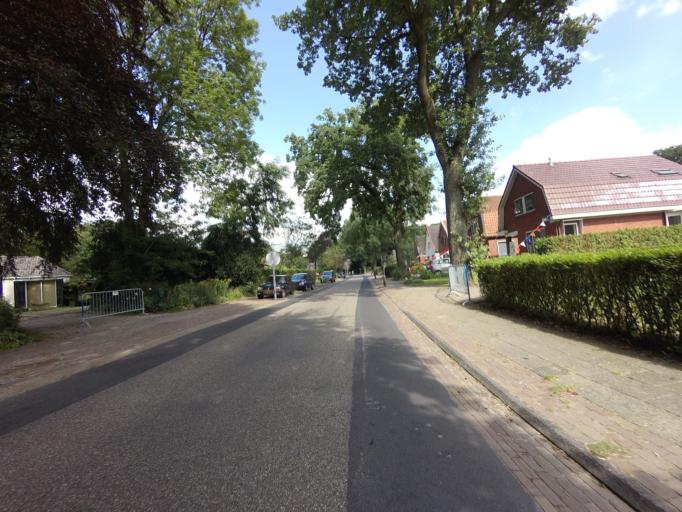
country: NL
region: Friesland
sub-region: Gemeente Heerenveen
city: Jubbega
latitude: 52.9824
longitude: 6.2181
